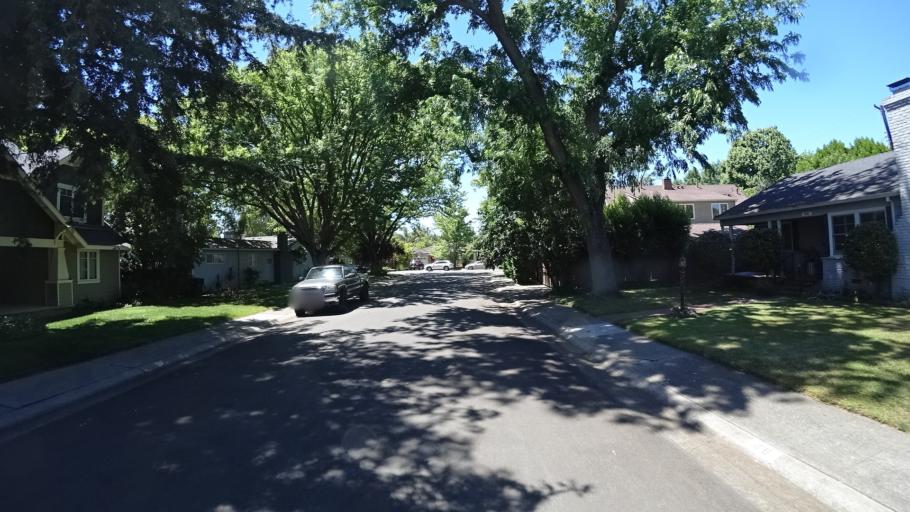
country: US
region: California
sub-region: Sacramento County
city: Sacramento
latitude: 38.5809
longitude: -121.4488
